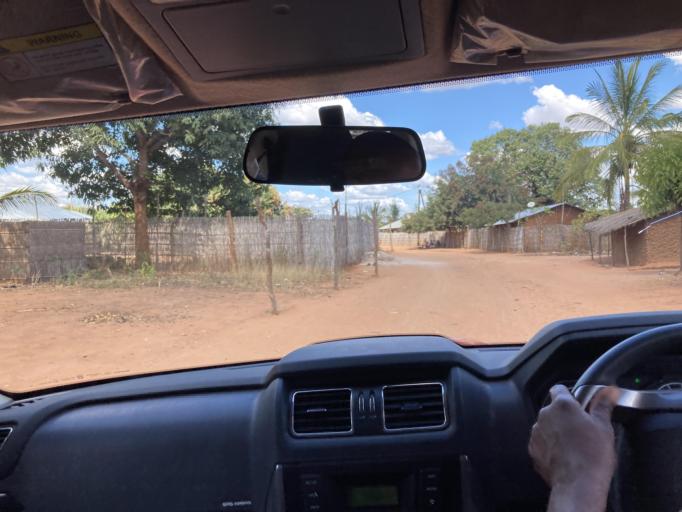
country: MZ
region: Cabo Delgado
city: Montepuez
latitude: -13.1454
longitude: 38.9846
